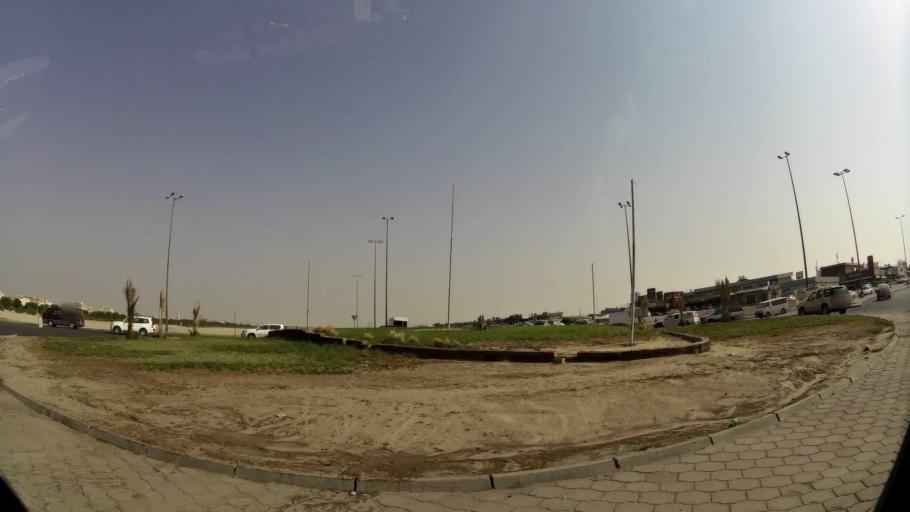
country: KW
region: Muhafazat al Jahra'
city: Al Jahra'
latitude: 29.3195
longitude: 47.6588
